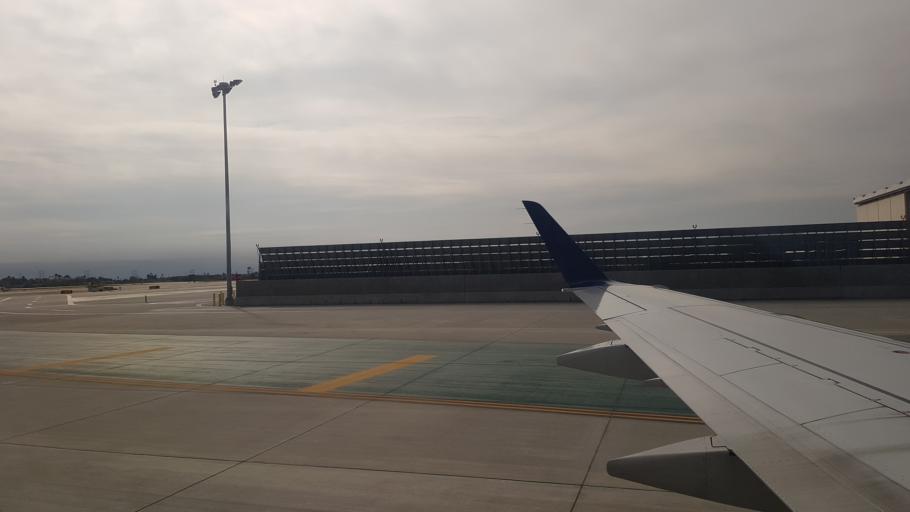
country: US
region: California
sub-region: Los Angeles County
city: El Segundo
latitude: 33.9393
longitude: -118.4125
